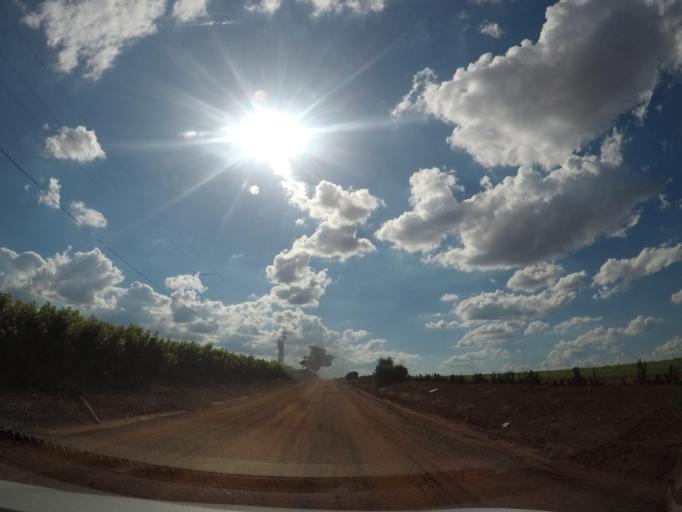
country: BR
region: Sao Paulo
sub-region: Sumare
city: Sumare
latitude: -22.8451
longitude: -47.3160
